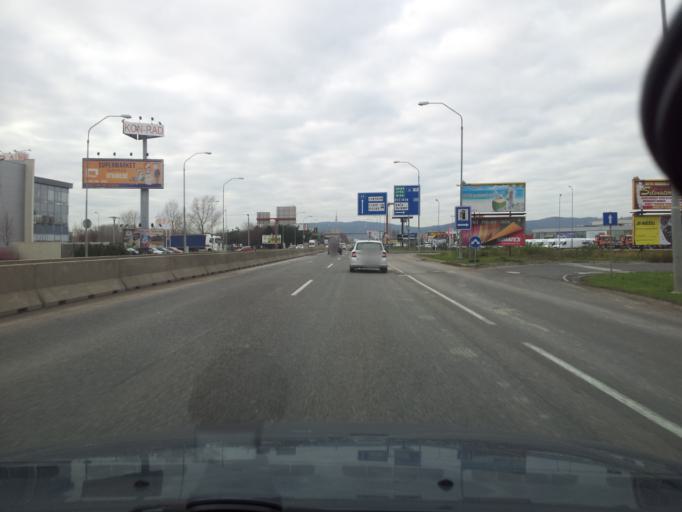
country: SK
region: Bratislavsky
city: Svaty Jur
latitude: 48.1899
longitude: 17.1979
